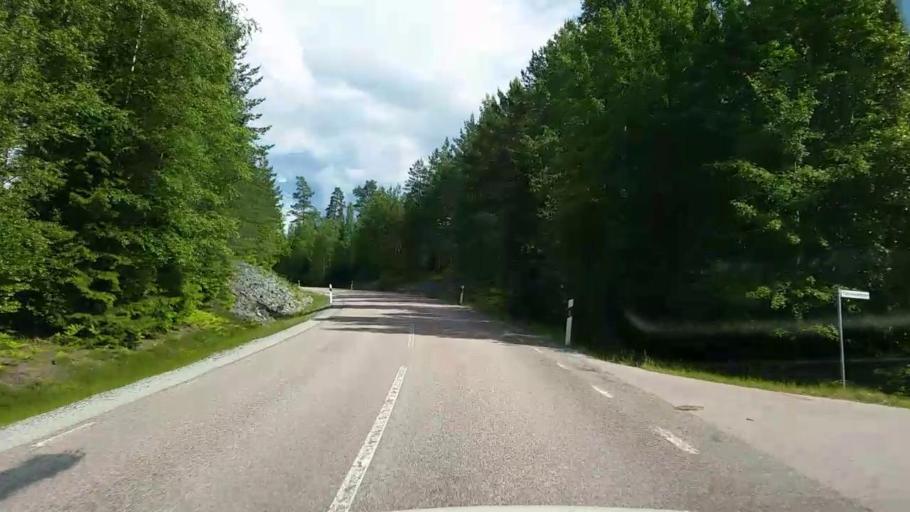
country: SE
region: Vaestmanland
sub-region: Fagersta Kommun
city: Fagersta
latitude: 59.9202
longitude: 15.8308
